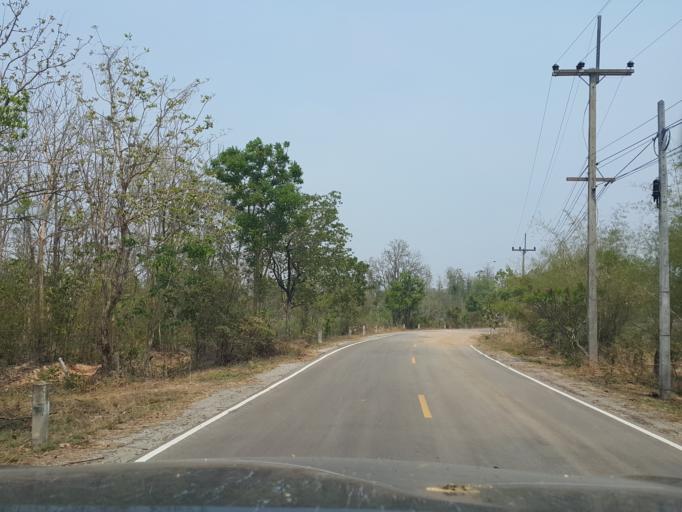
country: TH
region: Lampang
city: Mae Phrik
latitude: 17.5649
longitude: 99.0925
